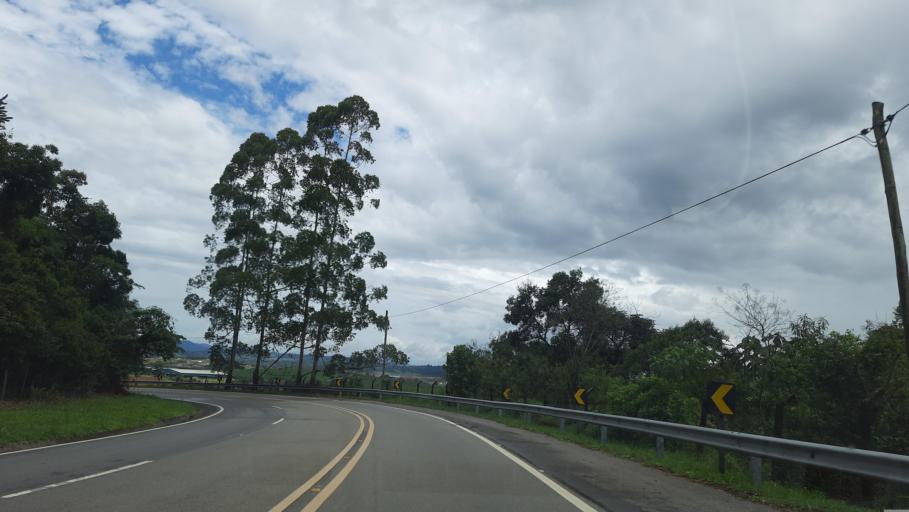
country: BR
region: Minas Gerais
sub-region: Pocos De Caldas
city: Pocos de Caldas
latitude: -21.8467
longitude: -46.6897
